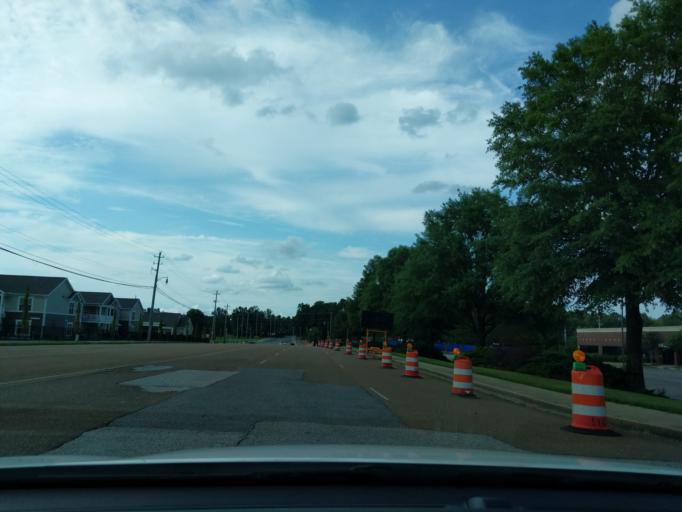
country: US
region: Tennessee
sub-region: Shelby County
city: Germantown
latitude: 35.0446
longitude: -89.7597
